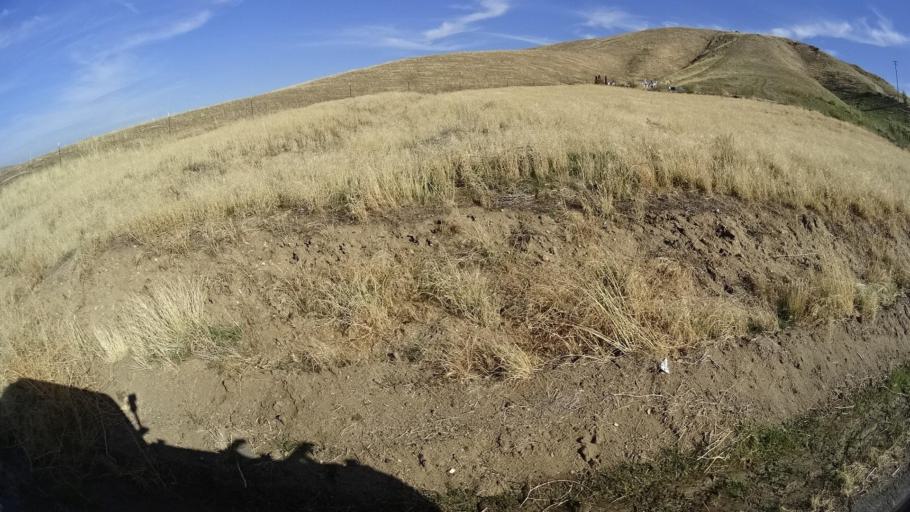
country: US
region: California
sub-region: Kern County
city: Lamont
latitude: 35.3901
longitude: -118.8172
